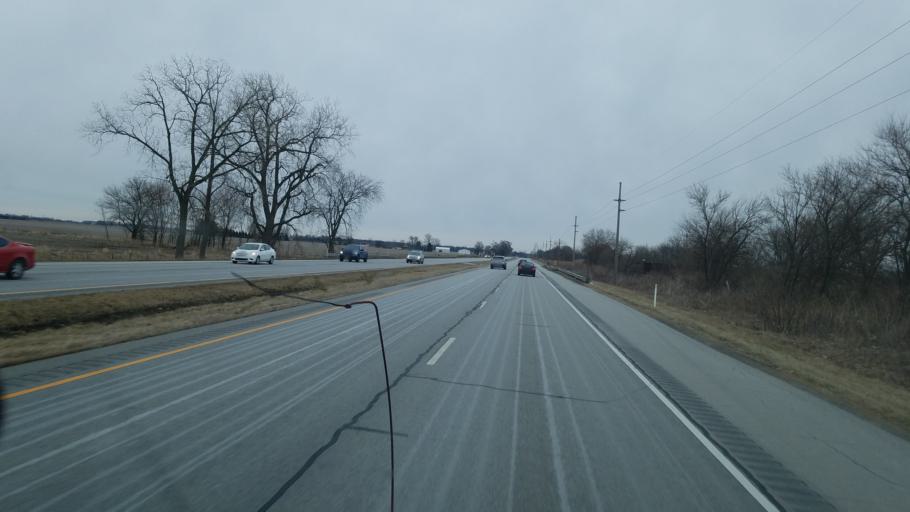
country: US
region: Indiana
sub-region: LaPorte County
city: Wanatah
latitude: 41.4396
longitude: -86.9644
